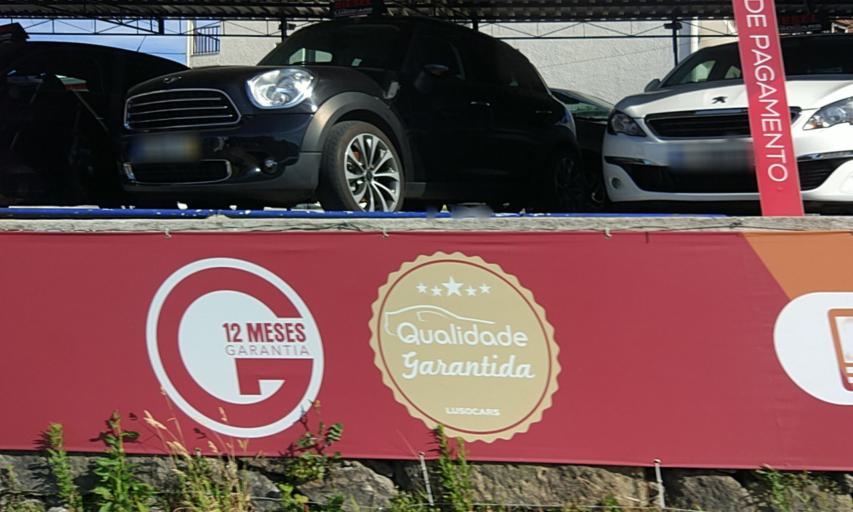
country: PT
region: Viseu
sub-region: Viseu
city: Viseu
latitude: 40.6654
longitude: -7.8945
